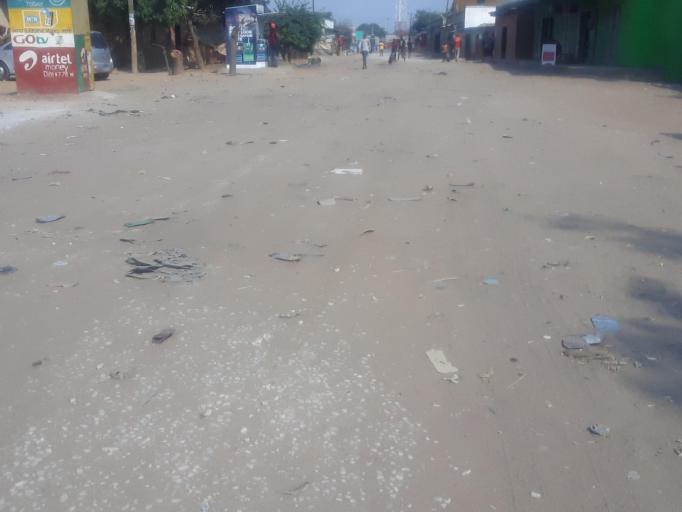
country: ZM
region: Lusaka
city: Lusaka
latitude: -15.3525
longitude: 28.2900
